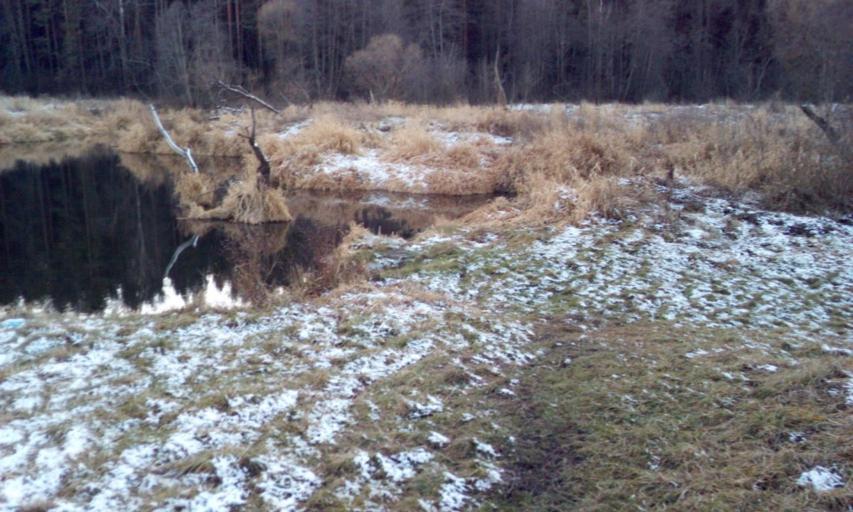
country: RU
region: Moskovskaya
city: Selyatino
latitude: 55.5348
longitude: 37.0017
